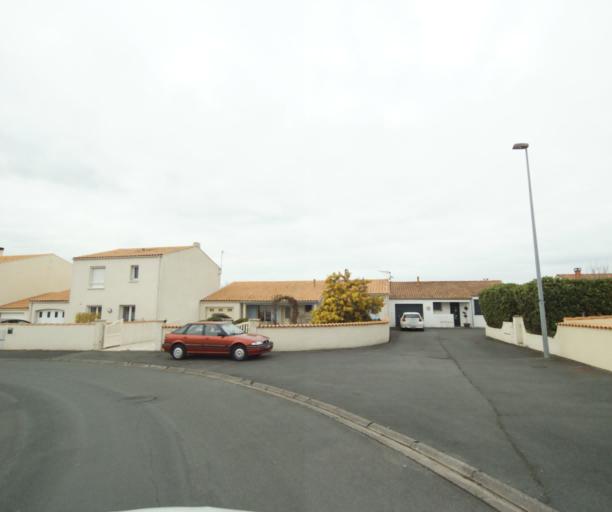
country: FR
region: Poitou-Charentes
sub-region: Departement de la Charente-Maritime
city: Lagord
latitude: 46.1888
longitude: -1.1505
